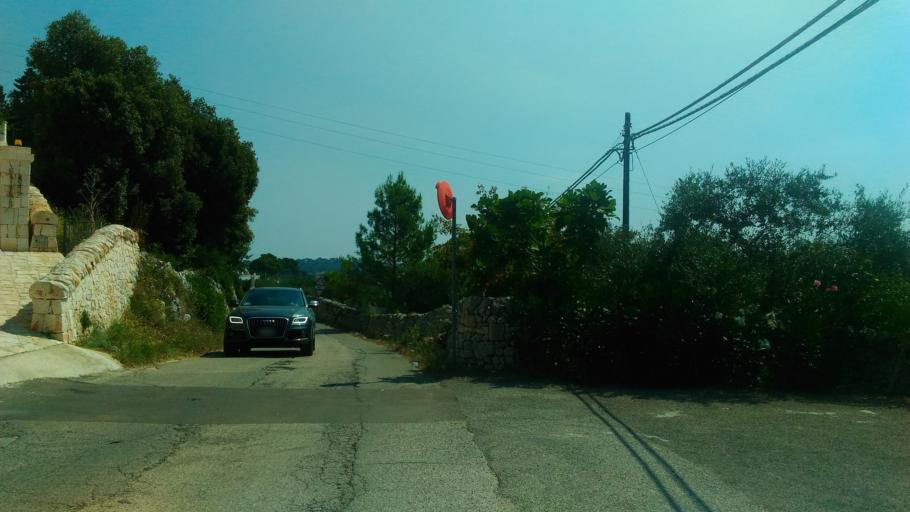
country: IT
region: Apulia
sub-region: Provincia di Bari
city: Locorotondo
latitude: 40.7517
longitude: 17.3423
